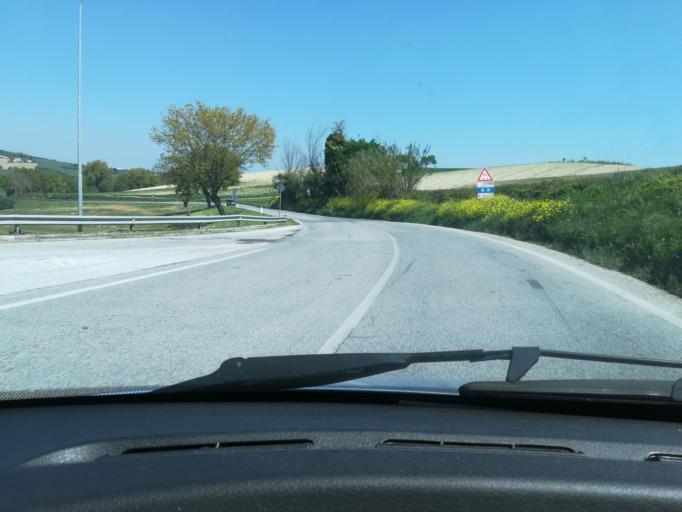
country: IT
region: The Marches
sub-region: Provincia di Macerata
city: Strada
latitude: 43.4022
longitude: 13.2047
